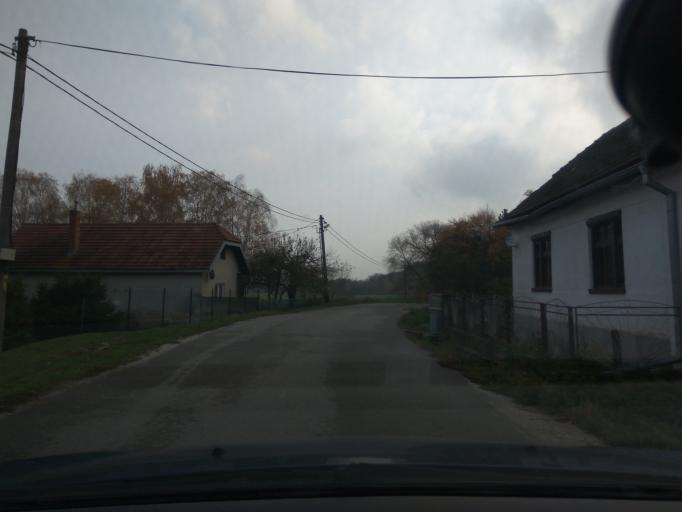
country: SK
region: Trnavsky
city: Vrbove
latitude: 48.6709
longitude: 17.6616
